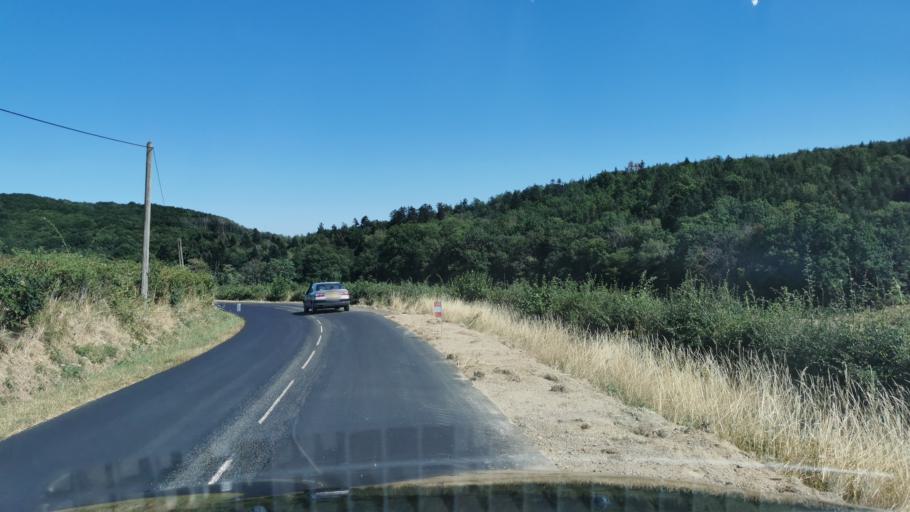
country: FR
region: Bourgogne
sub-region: Departement de Saone-et-Loire
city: Montcenis
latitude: 46.7956
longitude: 4.3665
